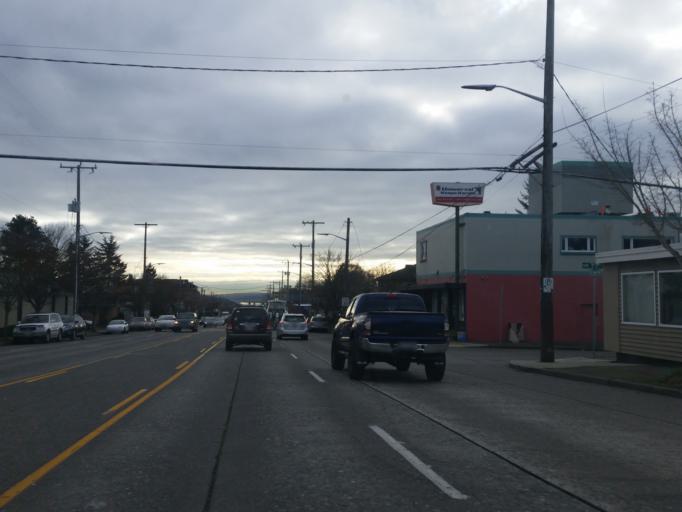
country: US
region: Washington
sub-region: King County
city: Shoreline
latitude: 47.6856
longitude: -122.3767
